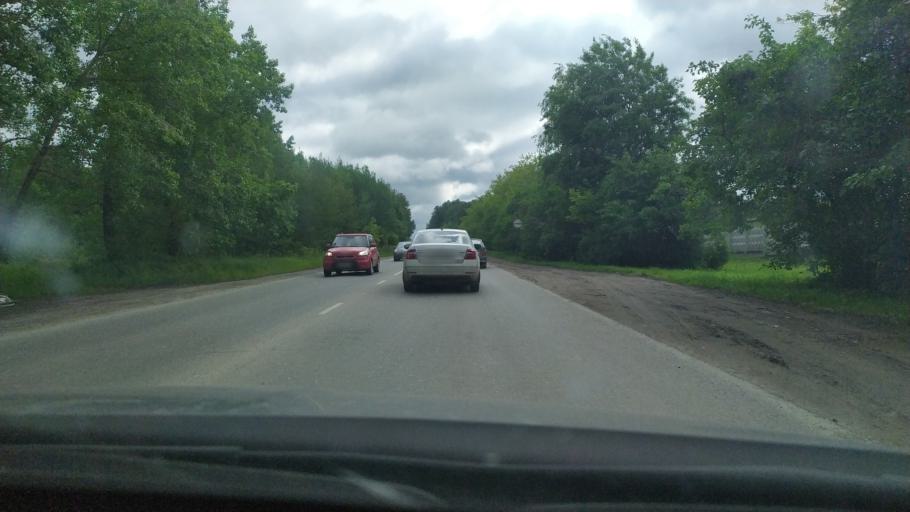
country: RU
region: Perm
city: Froly
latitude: 57.9753
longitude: 56.3256
